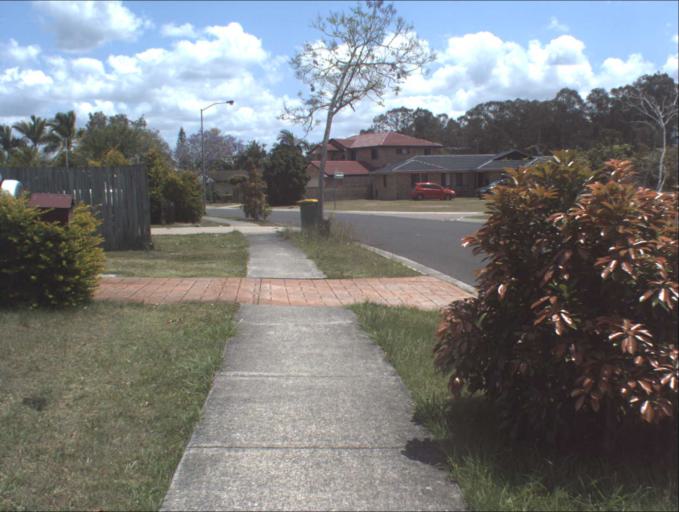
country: AU
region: Queensland
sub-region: Logan
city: Slacks Creek
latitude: -27.6678
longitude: 153.1512
